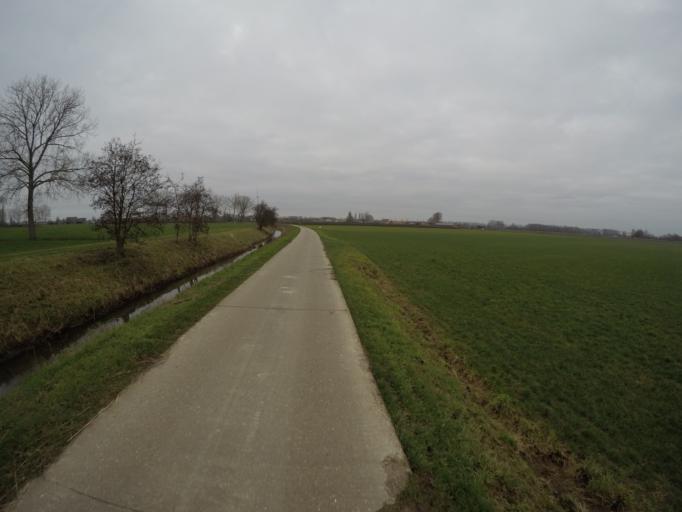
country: BE
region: Flanders
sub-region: Provincie Oost-Vlaanderen
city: Sint-Gillis-Waas
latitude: 51.2296
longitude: 4.1547
